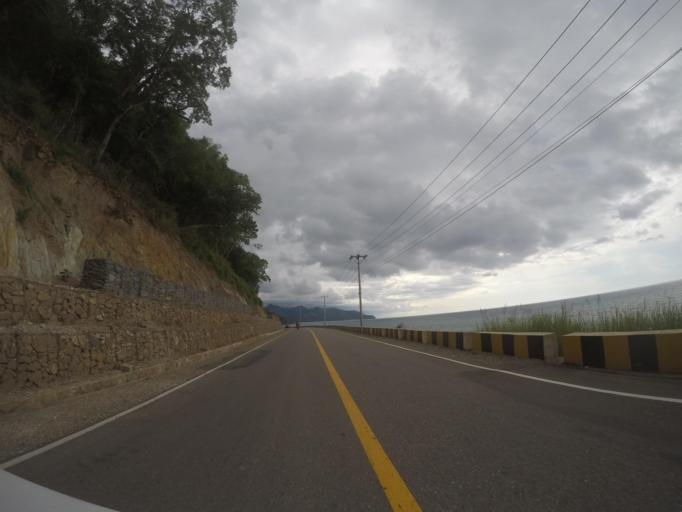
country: TL
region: Liquica
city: Maubara
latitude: -8.7985
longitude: 125.0958
